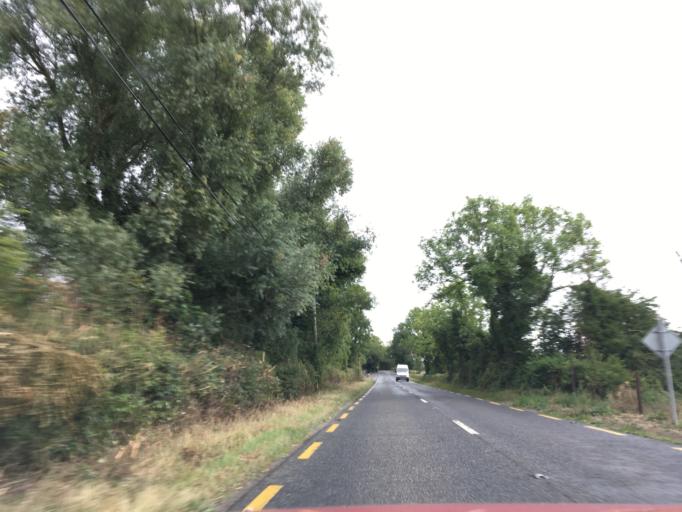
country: IE
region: Munster
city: Fethard
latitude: 52.4298
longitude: -7.7792
